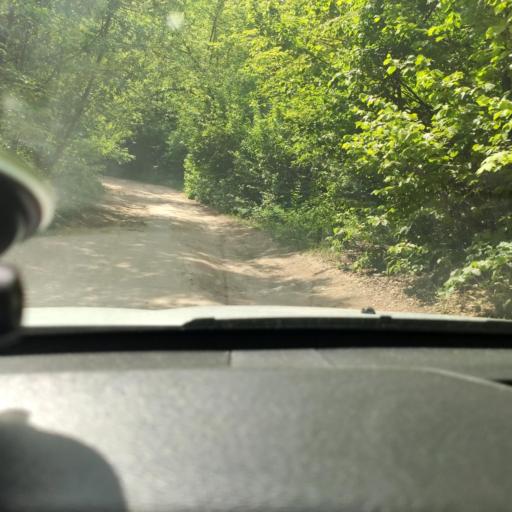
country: RU
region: Samara
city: Volzhskiy
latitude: 53.3378
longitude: 50.2042
